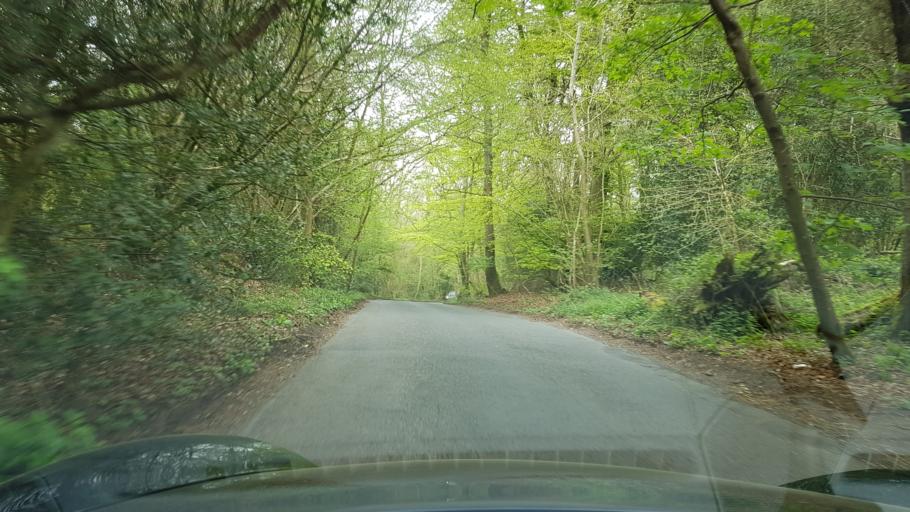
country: GB
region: England
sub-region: Surrey
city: East Horsley
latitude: 51.2301
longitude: -0.4048
